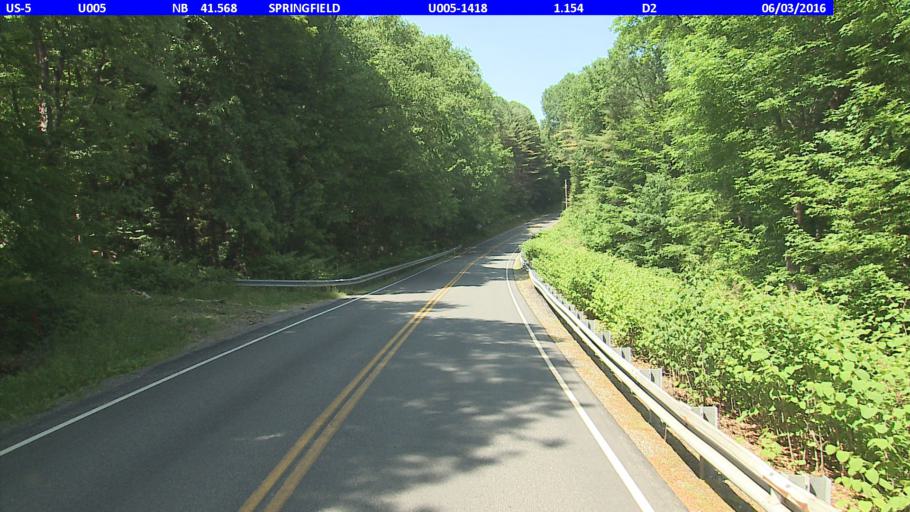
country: US
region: New Hampshire
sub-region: Sullivan County
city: Charlestown
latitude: 43.2496
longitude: -72.4408
